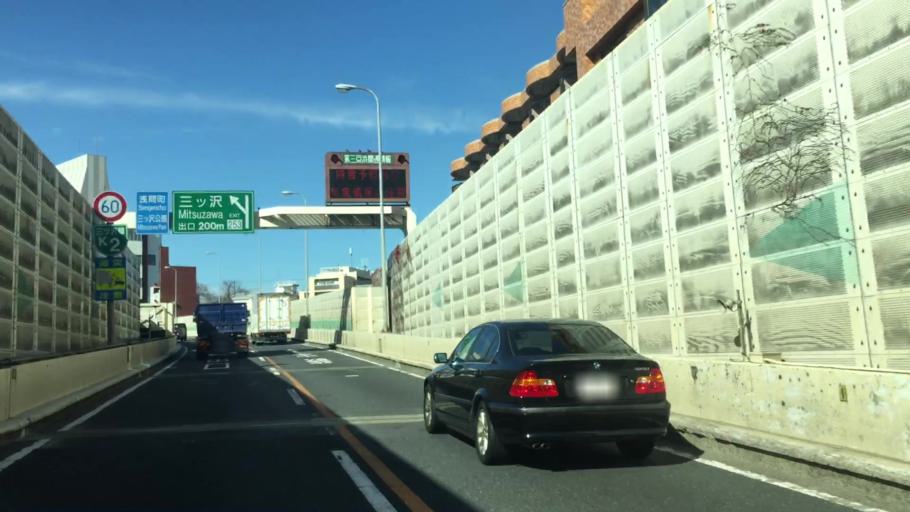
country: JP
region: Kanagawa
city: Yokohama
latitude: 35.4706
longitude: 139.6120
